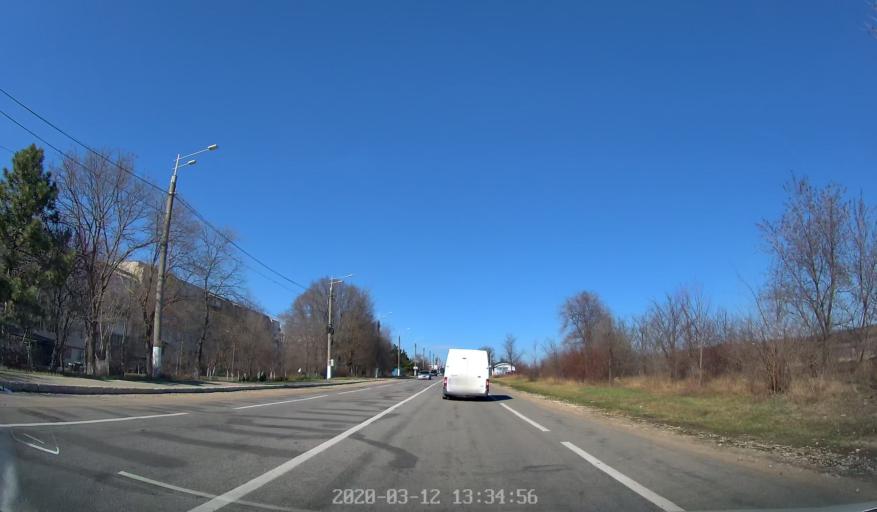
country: MD
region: Laloveni
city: Ialoveni
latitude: 46.9675
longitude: 28.7666
